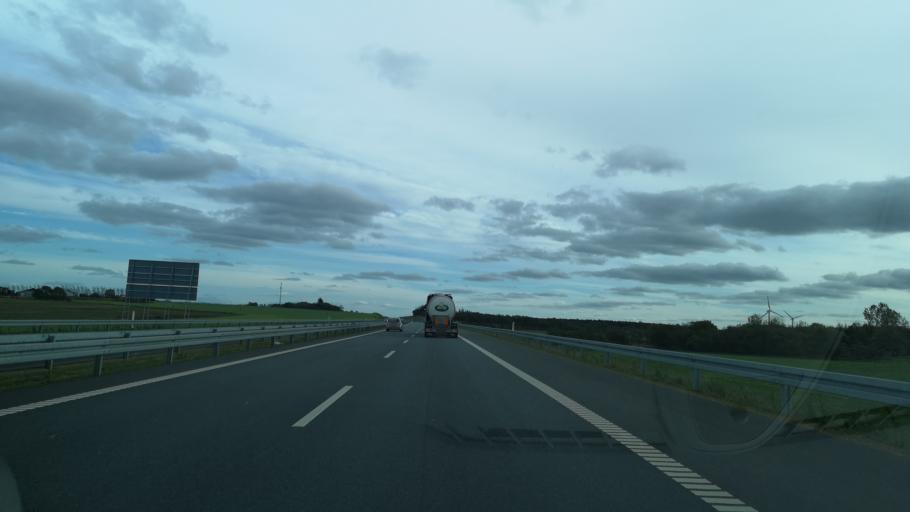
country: DK
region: Central Jutland
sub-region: Herning Kommune
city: Avlum
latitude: 56.2761
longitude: 8.7442
